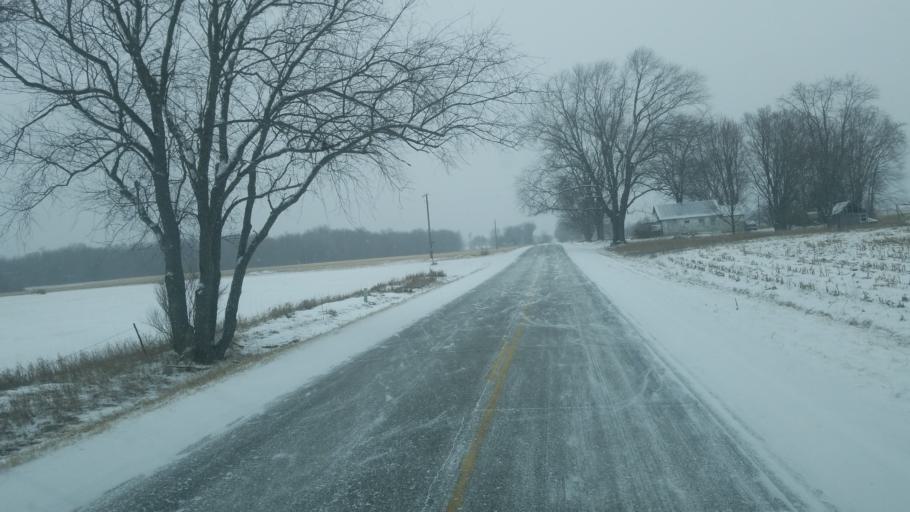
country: US
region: Michigan
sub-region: Mecosta County
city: Big Rapids
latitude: 43.7632
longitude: -85.4030
